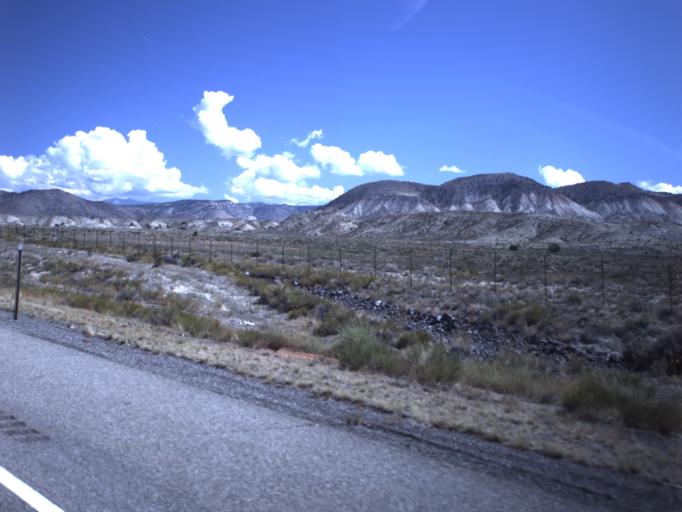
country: US
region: Utah
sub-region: Sevier County
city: Salina
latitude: 38.9170
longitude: -111.8806
